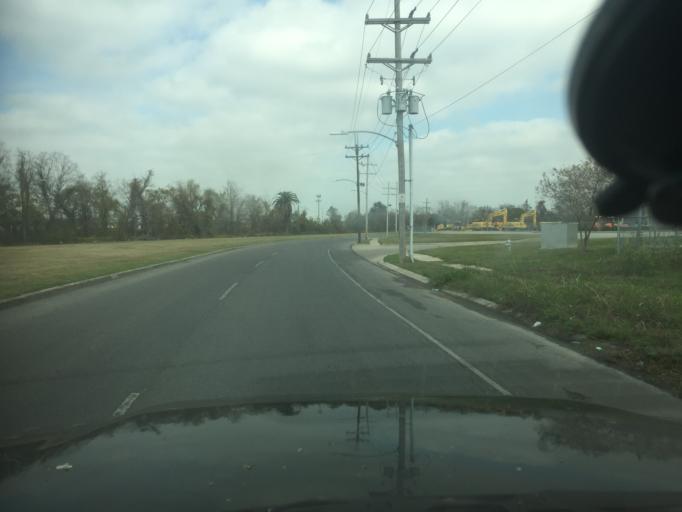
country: US
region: Louisiana
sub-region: Orleans Parish
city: New Orleans
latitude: 29.9991
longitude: -90.0406
